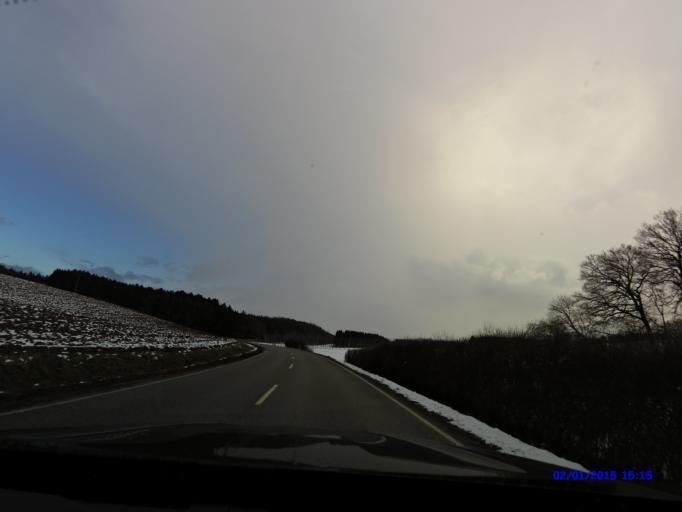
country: DE
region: Bavaria
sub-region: Lower Bavaria
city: Attenhofen
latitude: 48.6097
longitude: 11.8331
